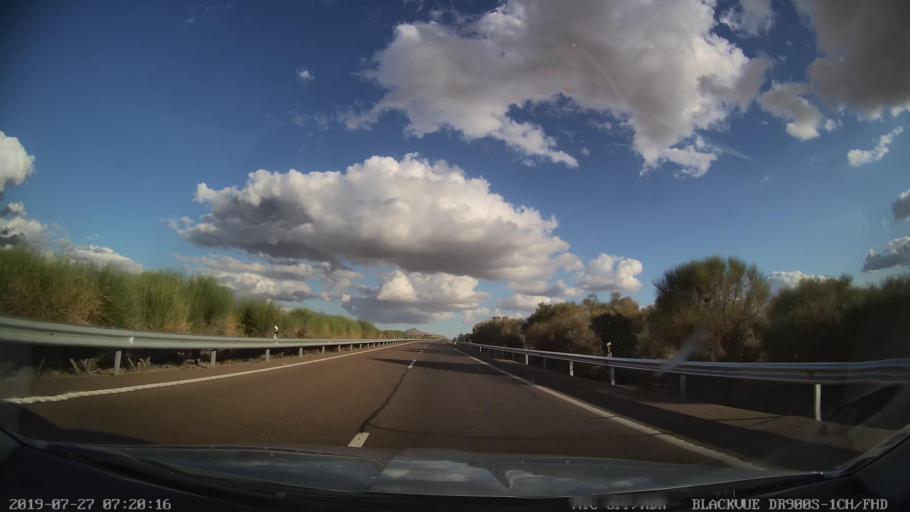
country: ES
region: Extremadura
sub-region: Provincia de Caceres
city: Santa Cruz de la Sierra
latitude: 39.3841
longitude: -5.8832
